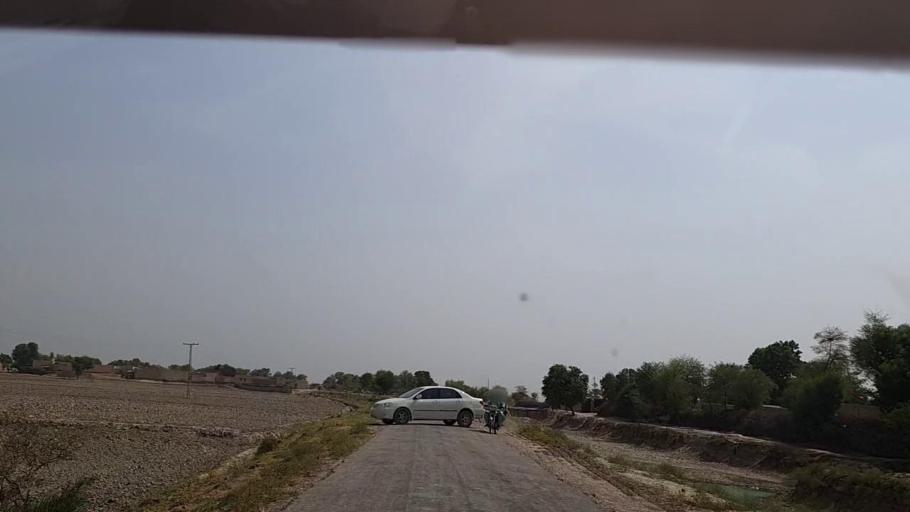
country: PK
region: Sindh
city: Khairpur Nathan Shah
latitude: 27.0681
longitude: 67.6878
